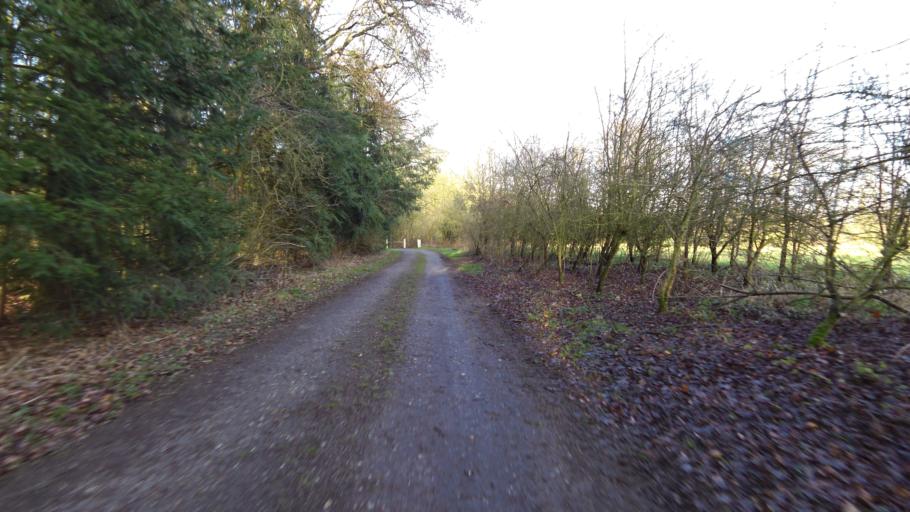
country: NL
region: Gelderland
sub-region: Gemeente Epe
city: Vaassen
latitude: 52.2583
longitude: 5.9268
